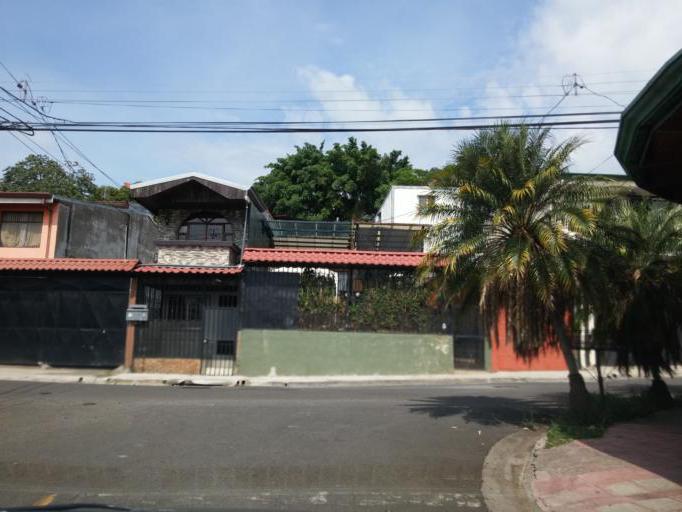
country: CR
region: Alajuela
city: Alajuela
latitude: 10.0112
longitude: -84.2192
